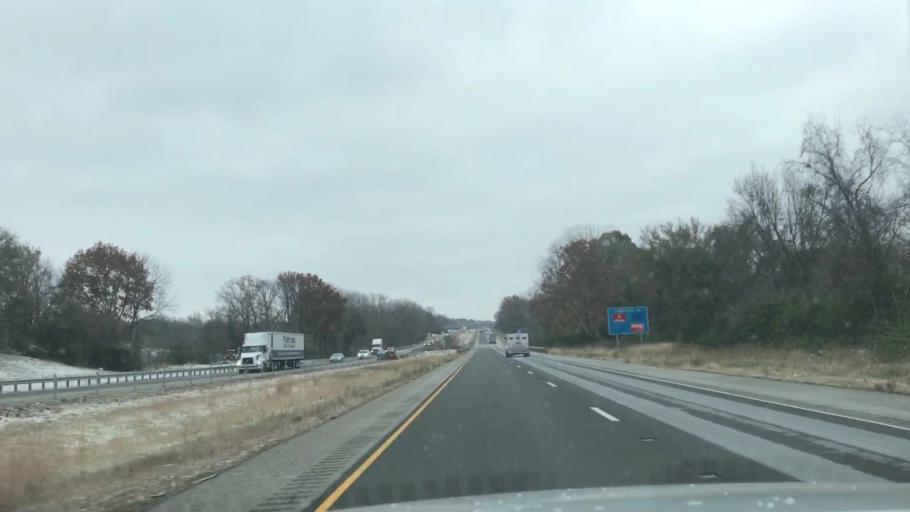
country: US
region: Illinois
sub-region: Madison County
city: Glen Carbon
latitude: 38.7567
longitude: -89.9841
